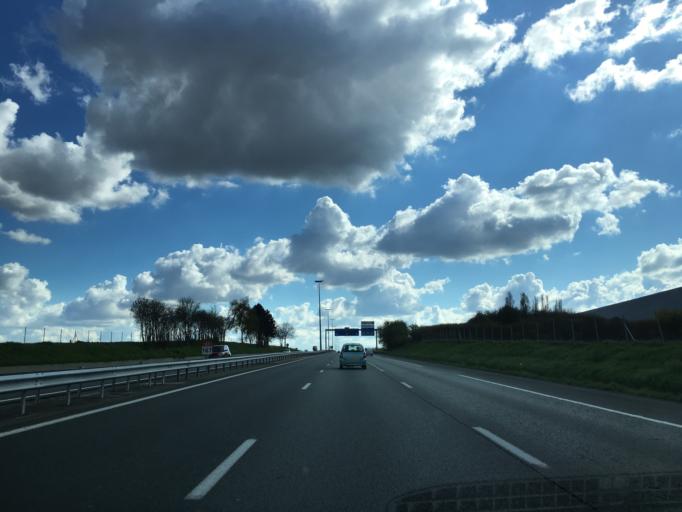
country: FR
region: Nord-Pas-de-Calais
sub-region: Departement du Pas-de-Calais
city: Fampoux
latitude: 50.2794
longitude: 2.8745
